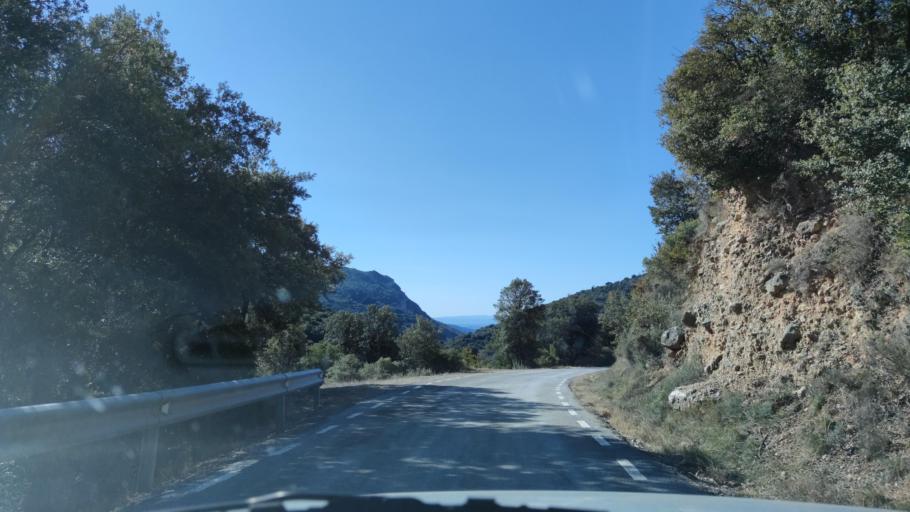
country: ES
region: Catalonia
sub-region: Provincia de Lleida
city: Llimiana
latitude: 42.0203
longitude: 1.0300
